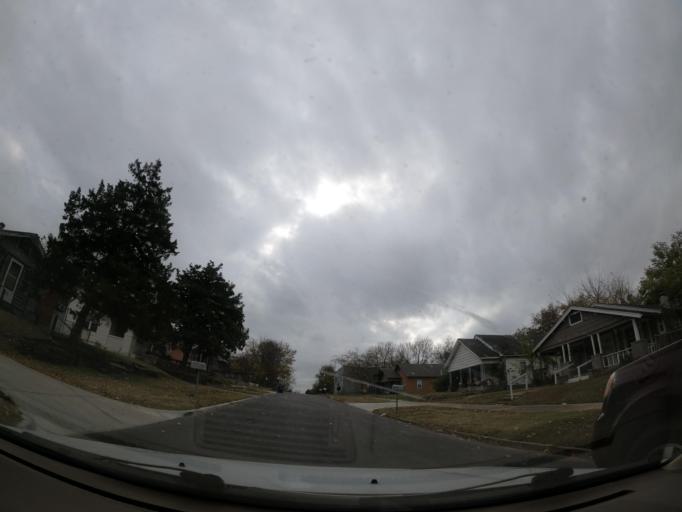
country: US
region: Oklahoma
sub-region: Tulsa County
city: Tulsa
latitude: 36.1636
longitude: -95.9622
